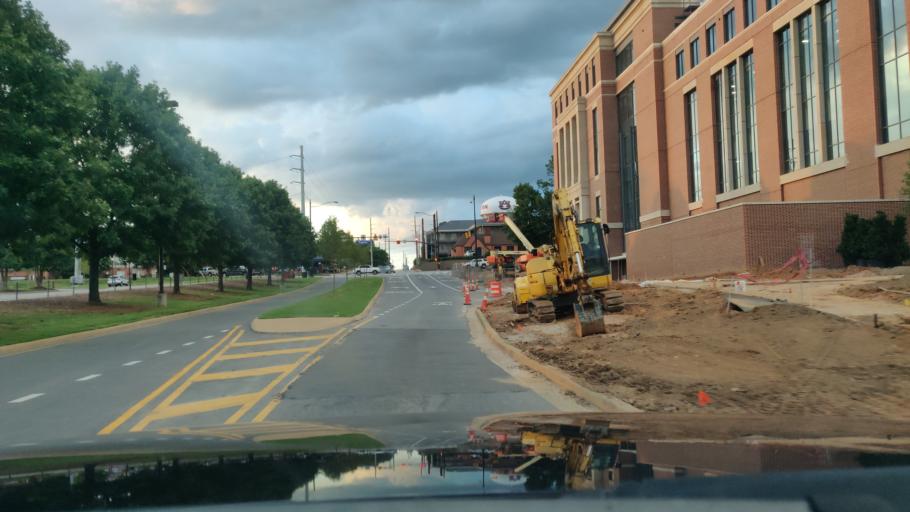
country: US
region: Alabama
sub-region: Lee County
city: Auburn
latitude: 32.6053
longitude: -85.4904
